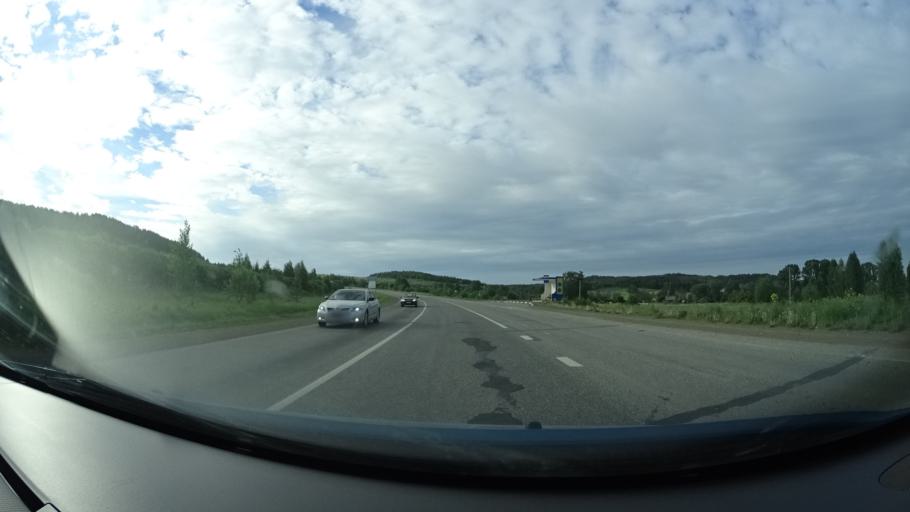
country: RU
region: Perm
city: Osa
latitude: 57.3315
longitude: 55.5853
